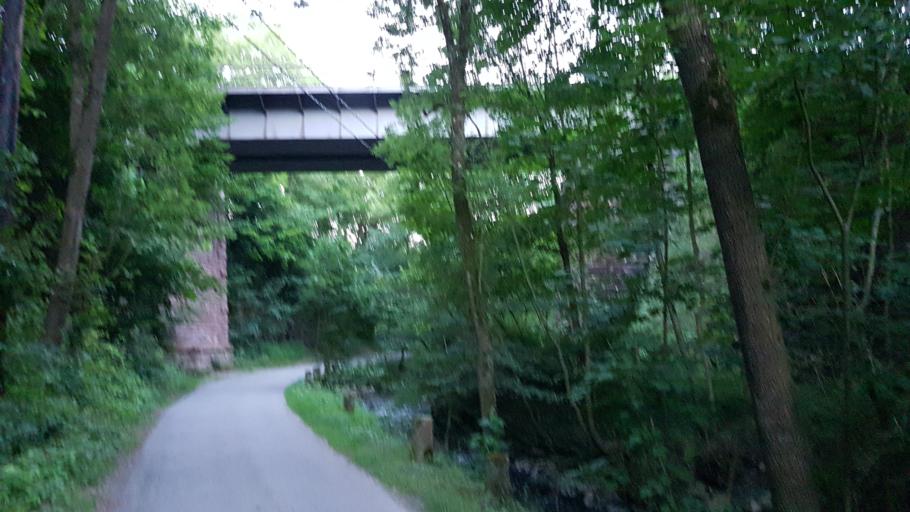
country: DE
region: Baden-Wuerttemberg
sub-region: Regierungsbezirk Stuttgart
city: Ditzingen
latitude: 48.8178
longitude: 9.0461
